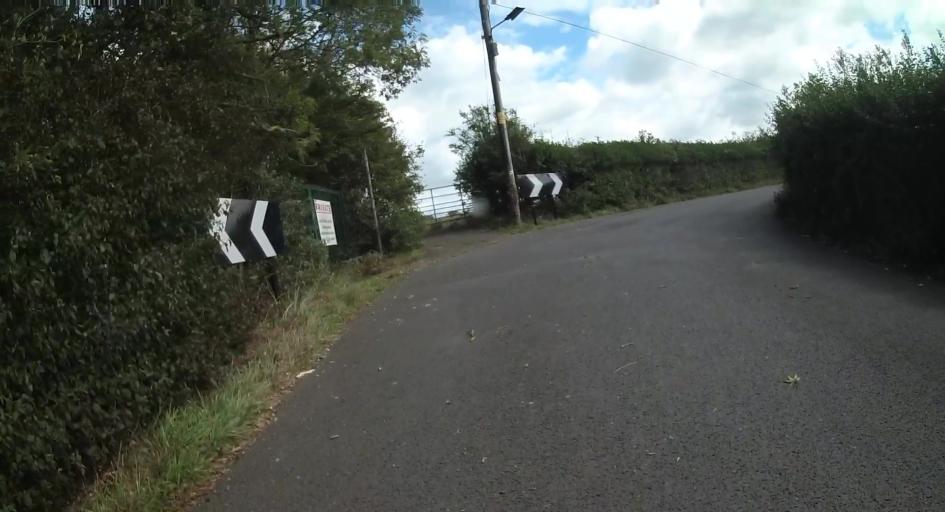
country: GB
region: England
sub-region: Isle of Wight
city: East Cowes
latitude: 50.7406
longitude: -1.2736
